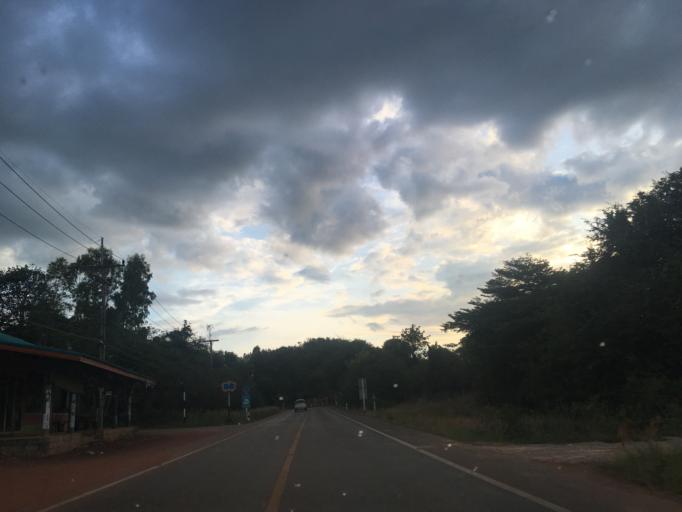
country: TH
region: Chanthaburi
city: Tha Mai
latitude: 12.6395
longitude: 101.8638
